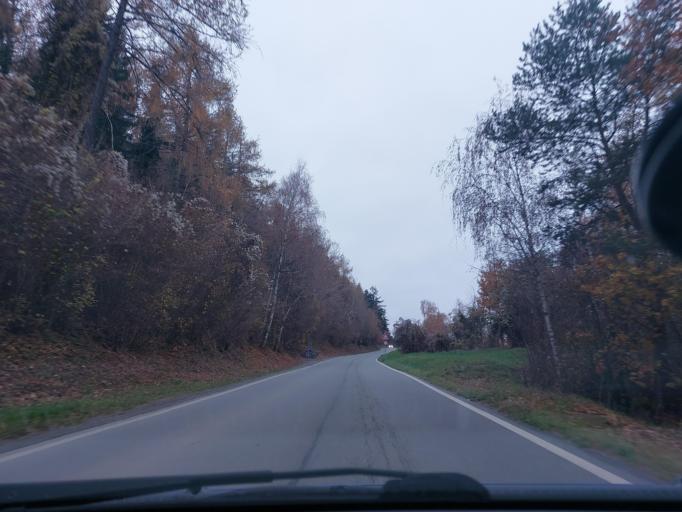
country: CH
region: Valais
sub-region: Conthey District
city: Basse-Nendaz
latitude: 46.1962
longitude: 7.2866
